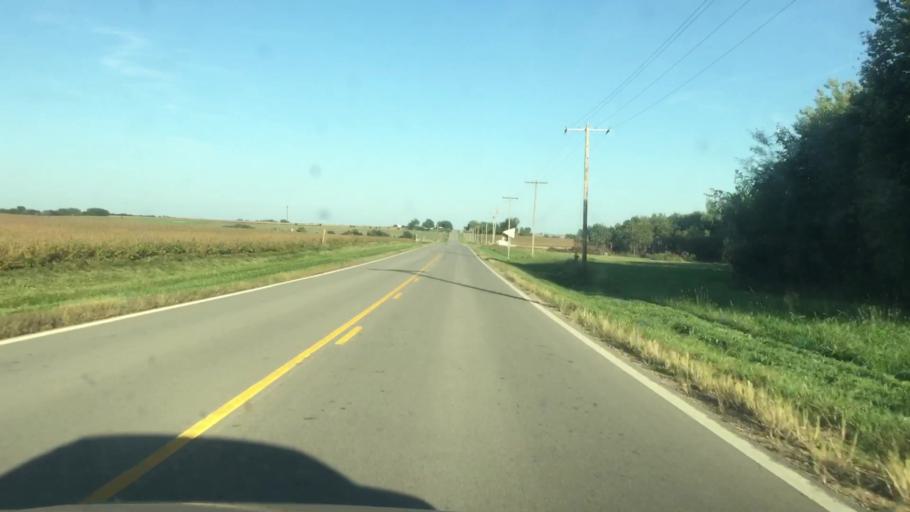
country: US
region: Kansas
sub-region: Brown County
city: Horton
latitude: 39.5876
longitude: -95.6049
